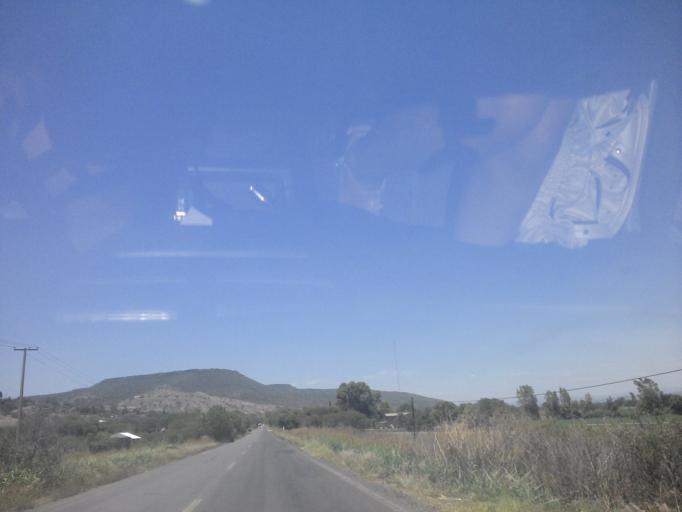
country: MX
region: Guanajuato
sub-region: San Francisco del Rincon
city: San Ignacio de Hidalgo
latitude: 20.9175
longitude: -101.9171
